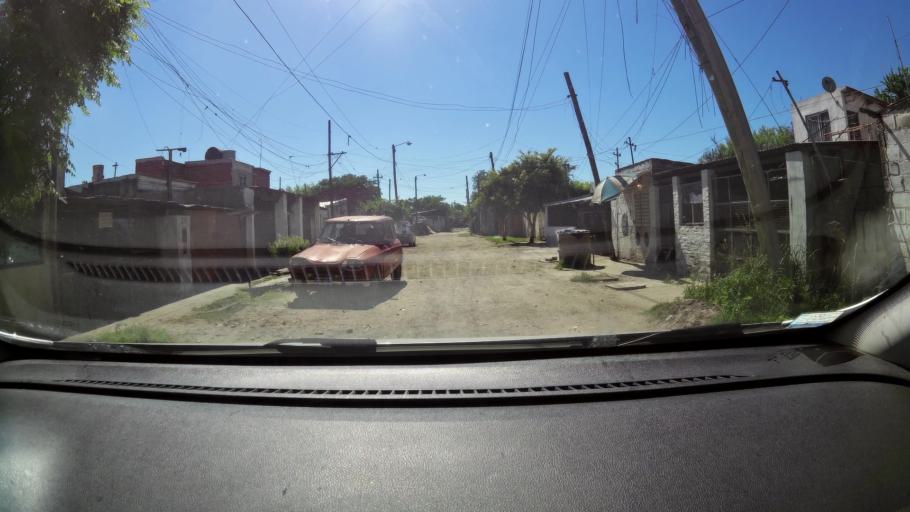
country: AR
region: Santa Fe
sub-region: Departamento de Rosario
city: Rosario
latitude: -32.9725
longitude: -60.6914
